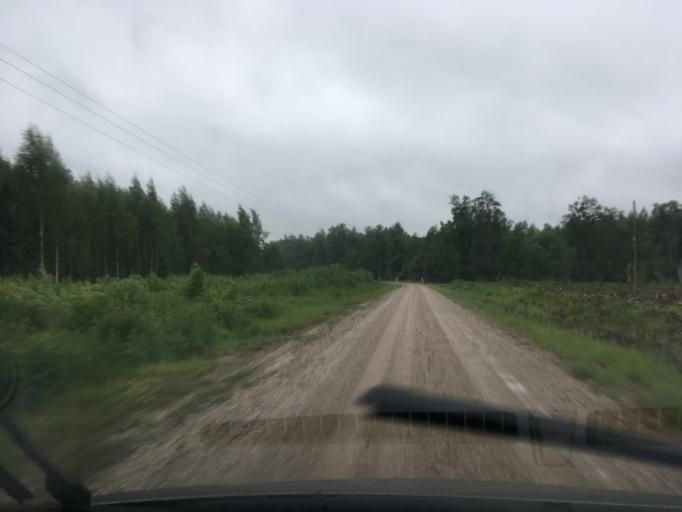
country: EE
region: Laeaene
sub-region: Lihula vald
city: Lihula
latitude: 58.6103
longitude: 23.8271
